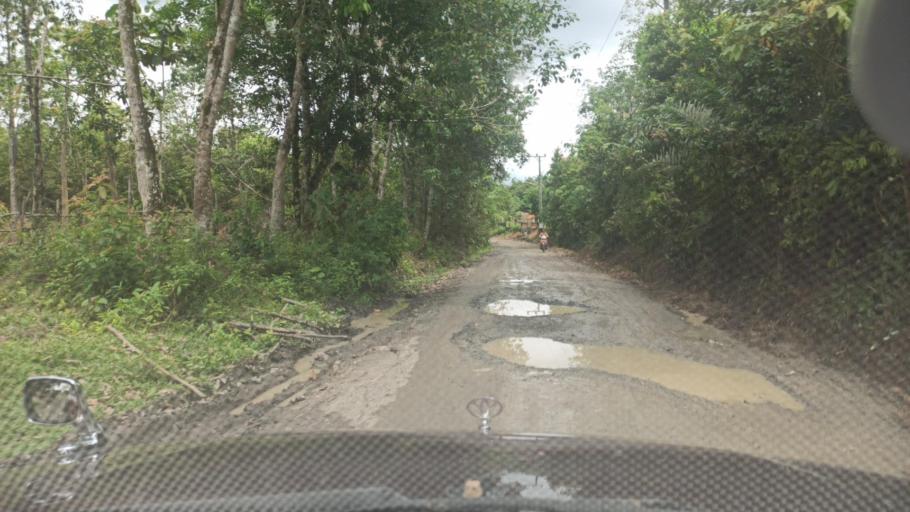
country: ID
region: South Sumatra
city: Gunungmenang
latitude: -3.0927
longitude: 103.9050
